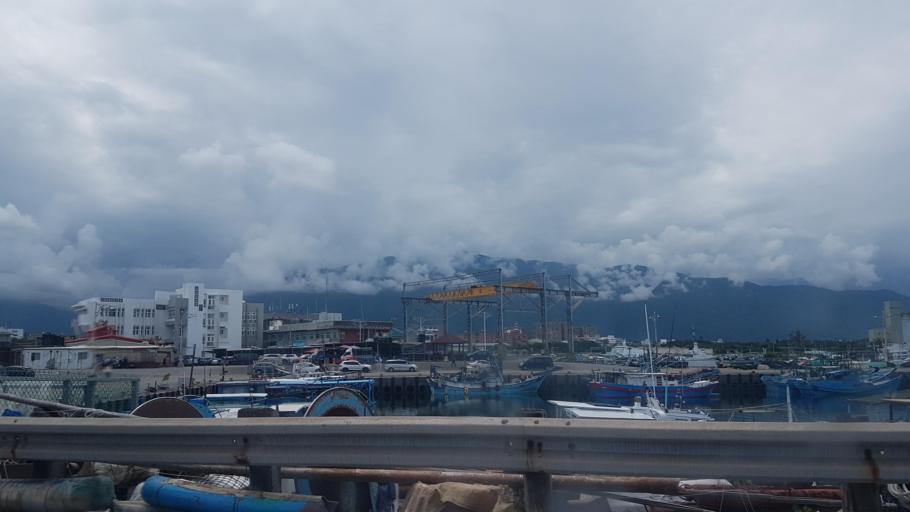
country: TW
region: Taiwan
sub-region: Hualien
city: Hualian
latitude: 23.9961
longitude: 121.6400
